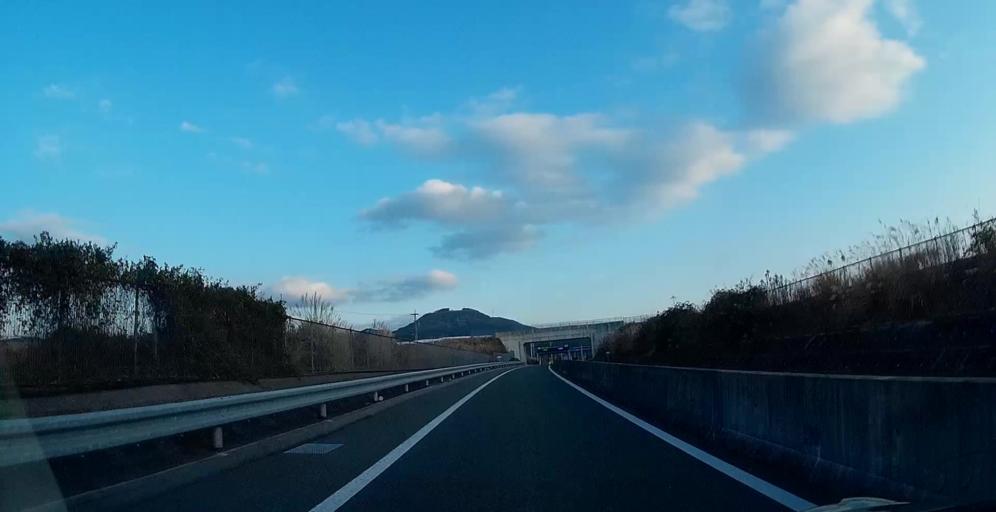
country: JP
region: Kumamoto
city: Kumamoto
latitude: 32.7526
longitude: 130.7954
